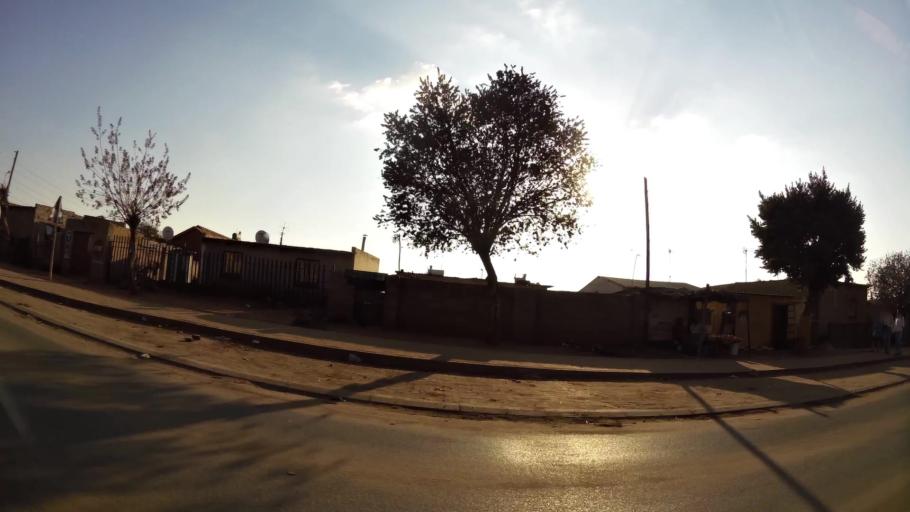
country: ZA
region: Gauteng
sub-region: Ekurhuleni Metropolitan Municipality
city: Tembisa
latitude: -25.9860
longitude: 28.2027
